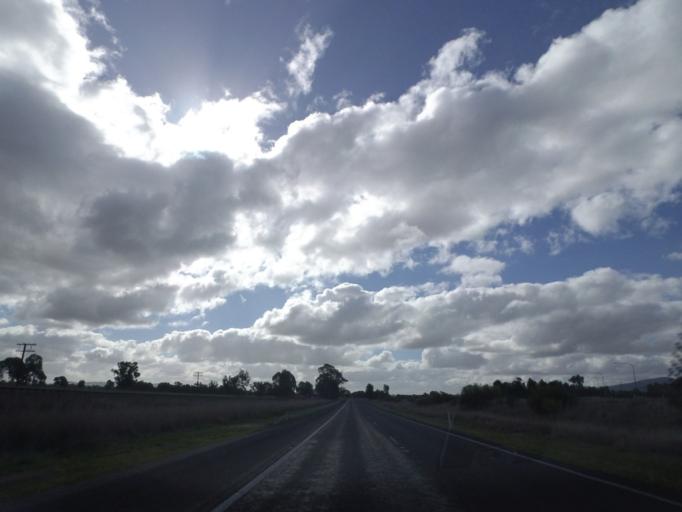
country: AU
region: New South Wales
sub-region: Greater Hume Shire
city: Jindera
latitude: -35.9359
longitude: 147.0027
